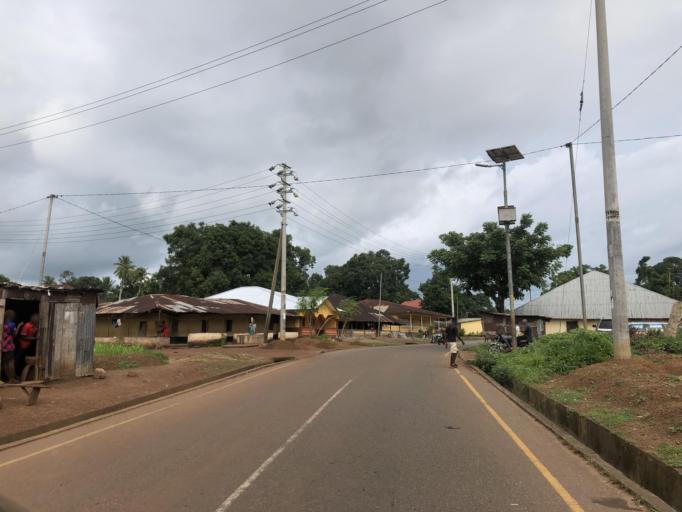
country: SL
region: Northern Province
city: Port Loko
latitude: 8.7677
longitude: -12.7862
